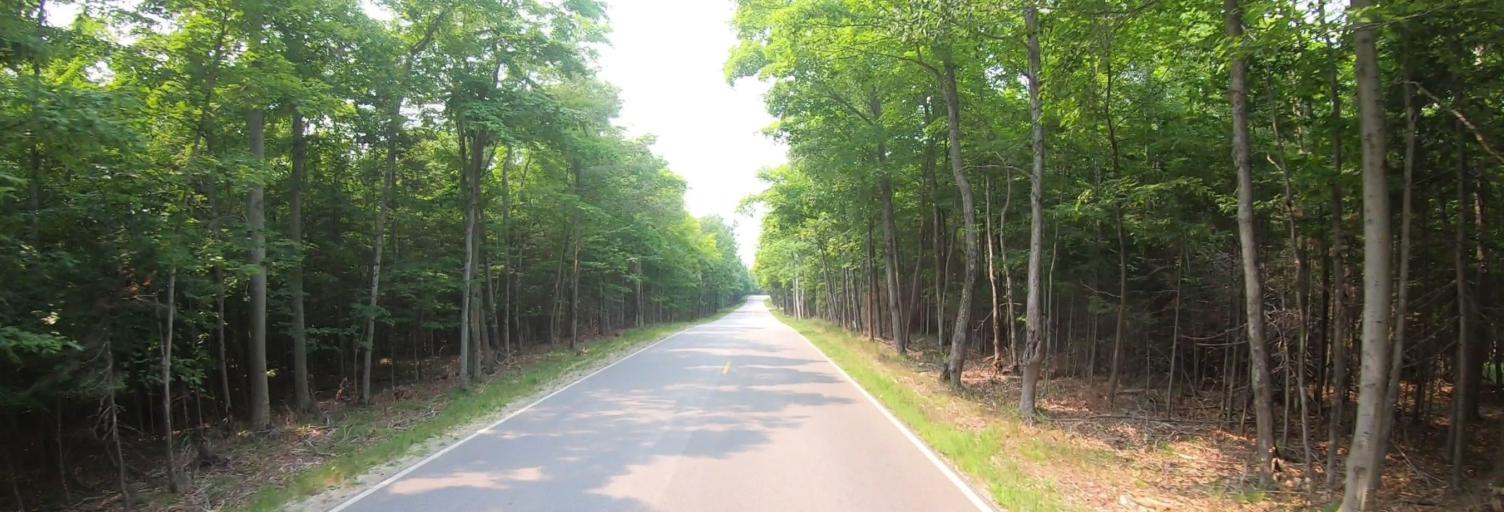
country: CA
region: Ontario
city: Thessalon
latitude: 46.0167
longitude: -83.7134
